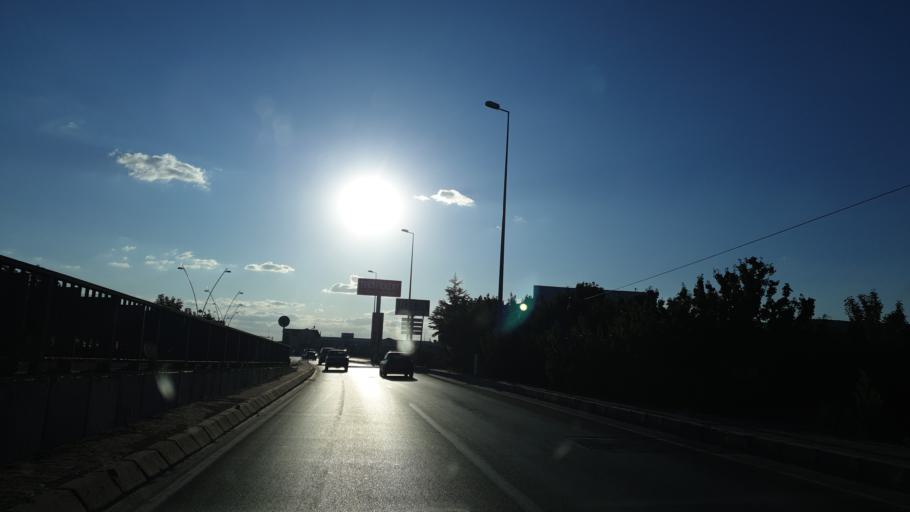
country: TR
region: Kayseri
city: Kocasinan
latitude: 38.7500
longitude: 35.5467
